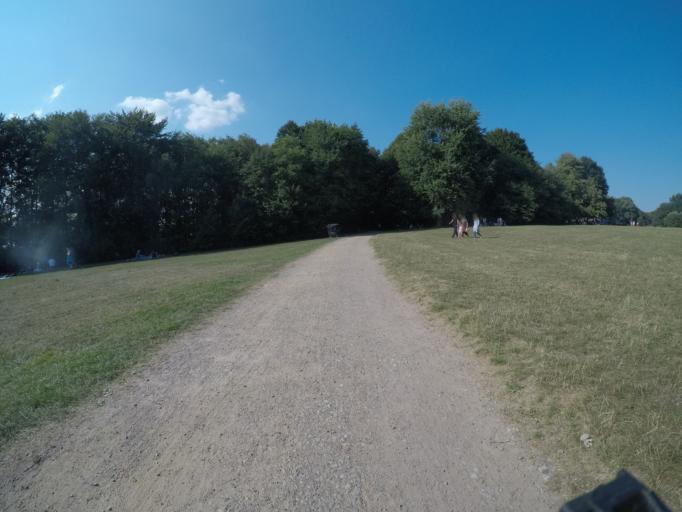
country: DE
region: Schleswig-Holstein
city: Barsbuettel
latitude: 53.5592
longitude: 10.1452
